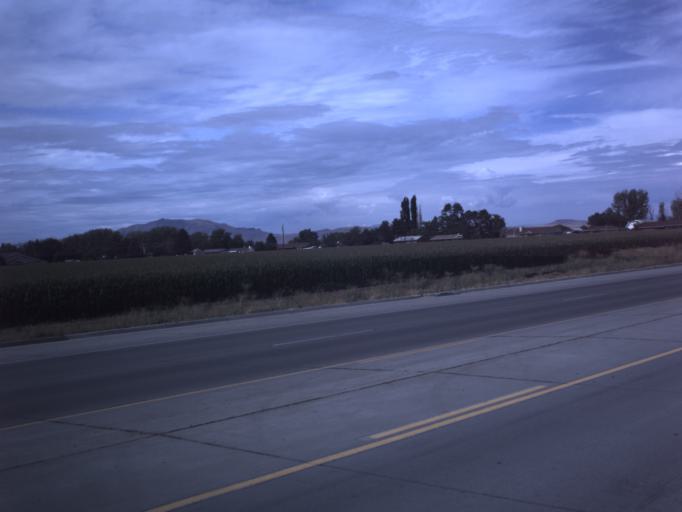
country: US
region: Utah
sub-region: Davis County
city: Syracuse
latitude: 41.1106
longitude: -112.0608
